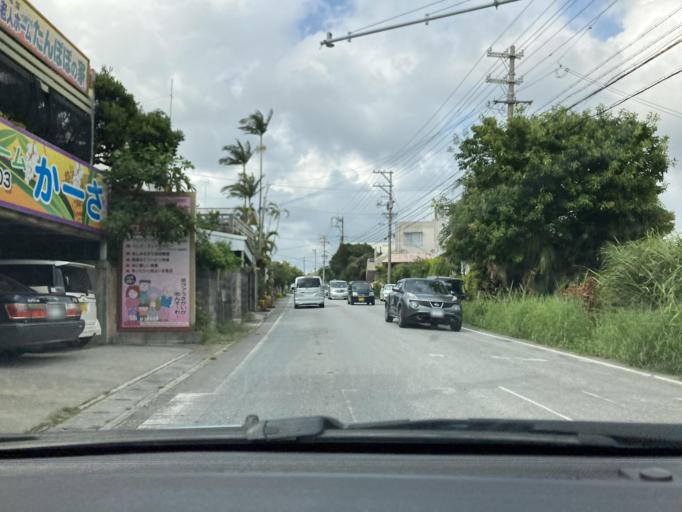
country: JP
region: Okinawa
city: Chatan
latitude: 26.2863
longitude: 127.7864
